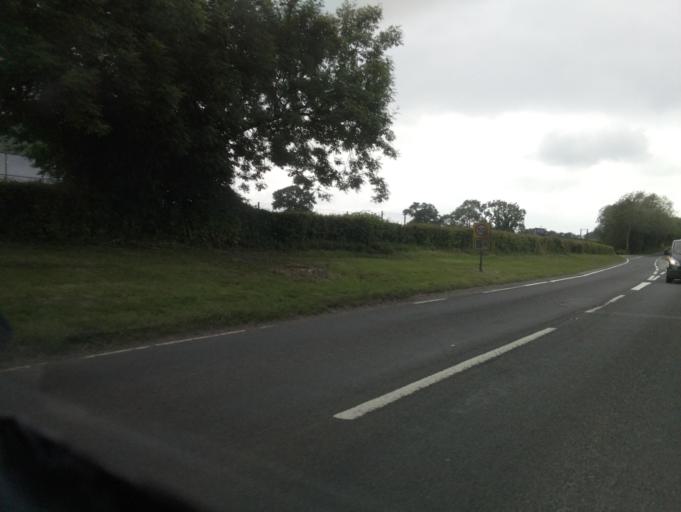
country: GB
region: England
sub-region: Derbyshire
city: Rodsley
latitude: 52.9198
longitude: -1.7606
